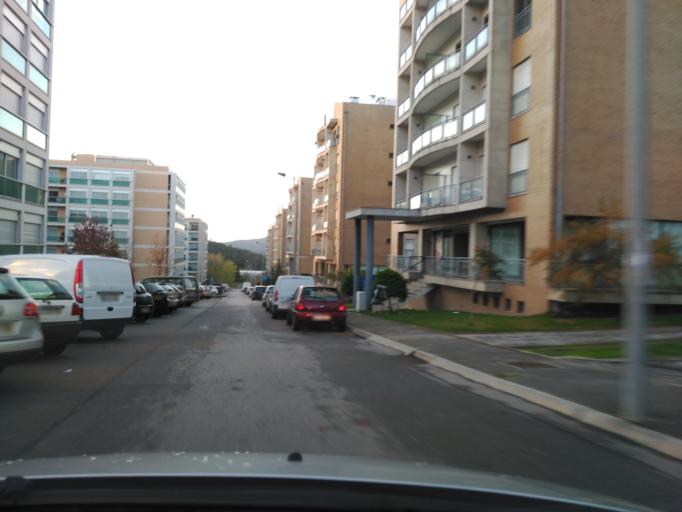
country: PT
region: Braga
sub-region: Braga
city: Braga
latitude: 41.5311
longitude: -8.4115
